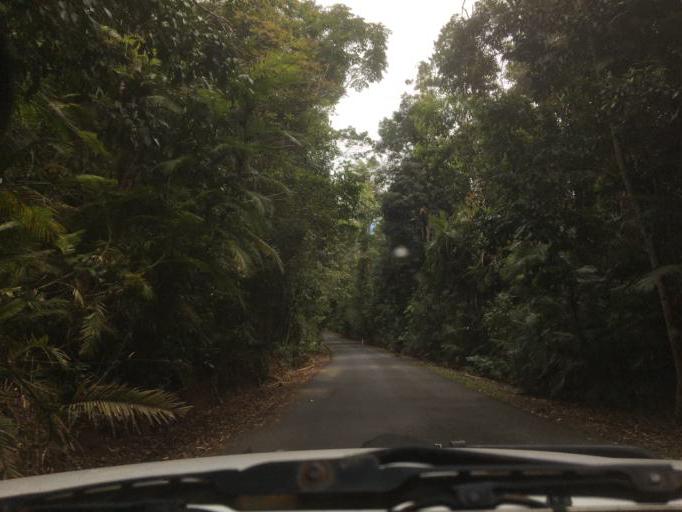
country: AU
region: Queensland
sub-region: Tablelands
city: Tolga
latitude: -17.2803
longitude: 145.6211
